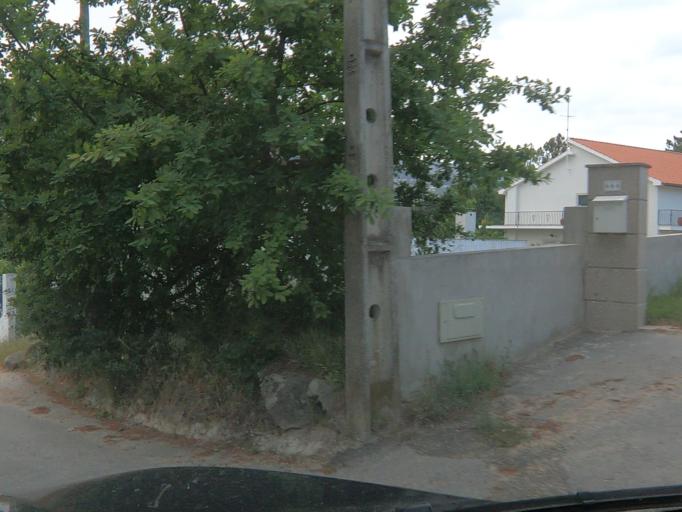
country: PT
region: Vila Real
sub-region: Vila Real
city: Vila Real
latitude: 41.3243
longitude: -7.7341
